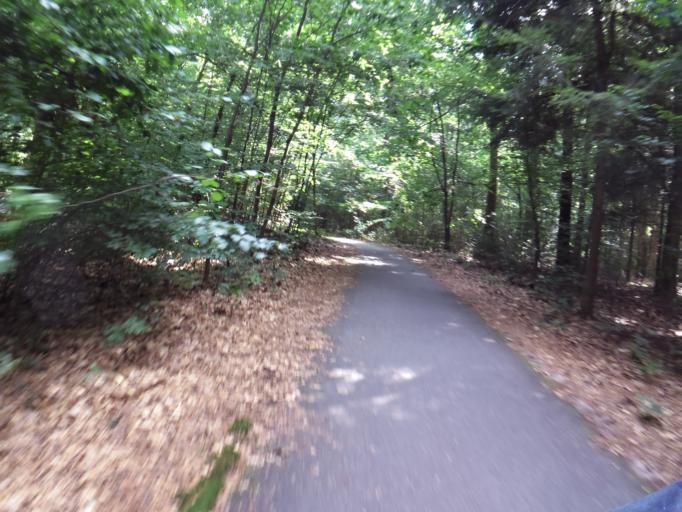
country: NL
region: Drenthe
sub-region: Gemeente Borger-Odoorn
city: Borger
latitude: 52.9754
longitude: 6.7548
